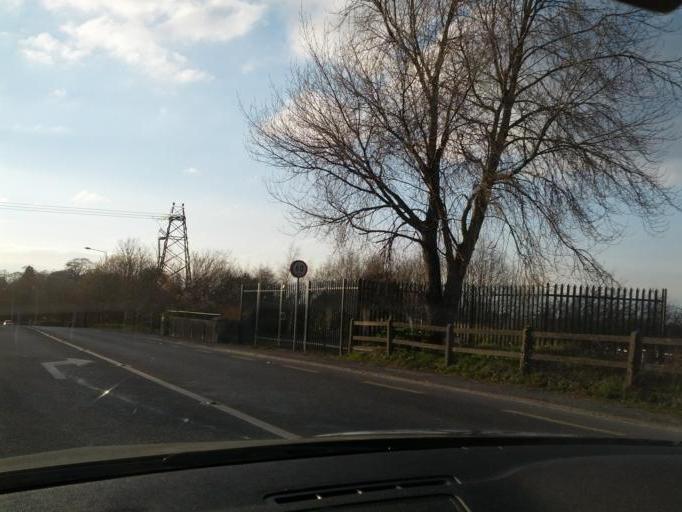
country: IE
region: Munster
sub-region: North Tipperary
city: Nenagh
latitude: 52.8657
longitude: -8.1796
